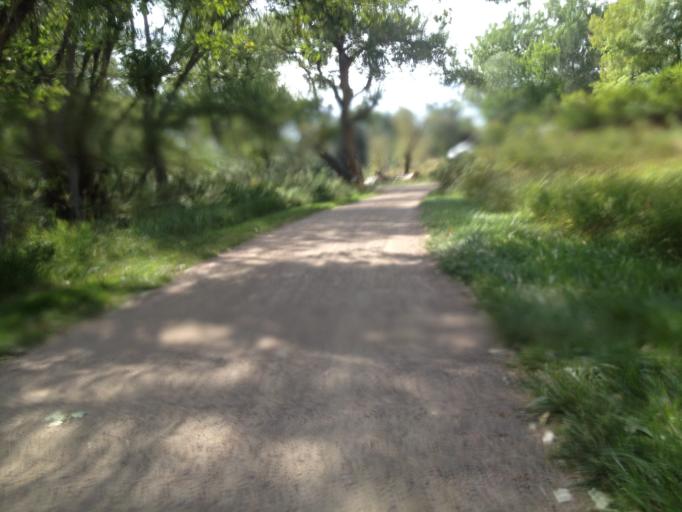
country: US
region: Colorado
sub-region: Boulder County
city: Louisville
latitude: 39.9793
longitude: -105.1086
